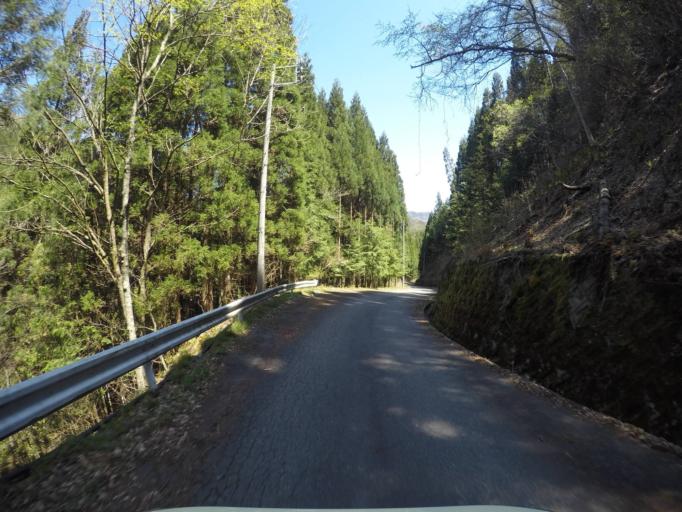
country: JP
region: Gifu
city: Takayama
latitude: 36.1624
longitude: 137.4382
